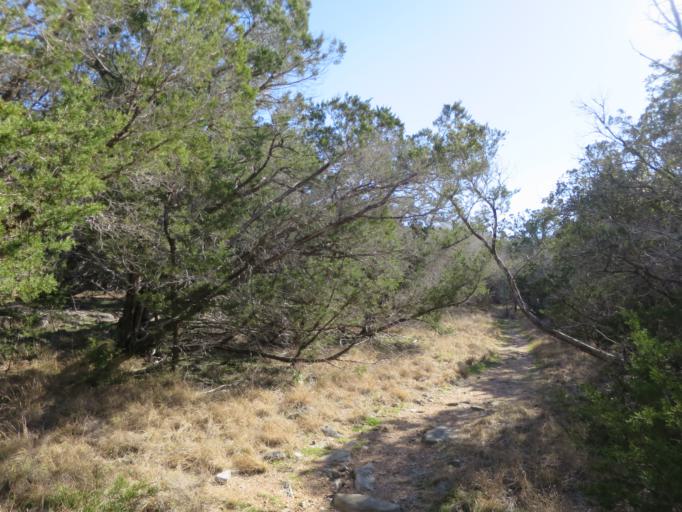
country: US
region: Texas
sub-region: Llano County
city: Kingsland
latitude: 30.6844
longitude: -98.3551
